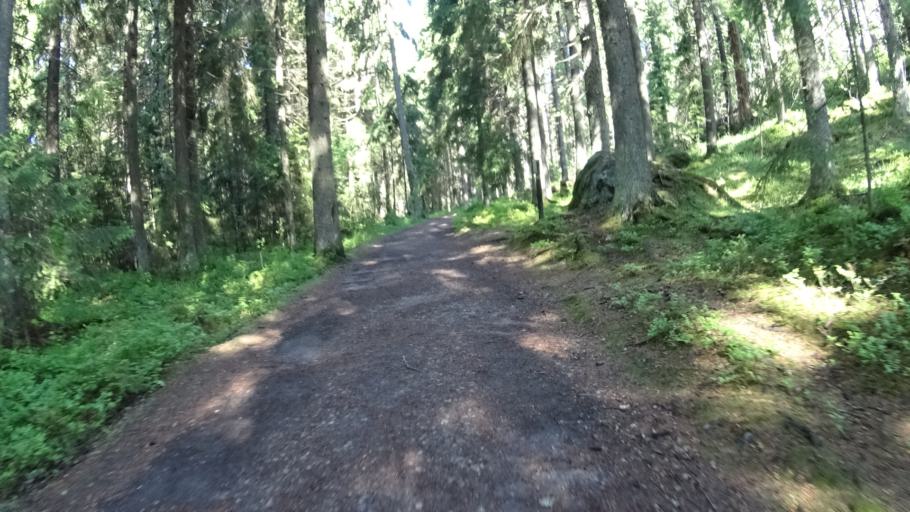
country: FI
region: Uusimaa
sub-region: Helsinki
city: Kauniainen
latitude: 60.3227
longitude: 24.6900
